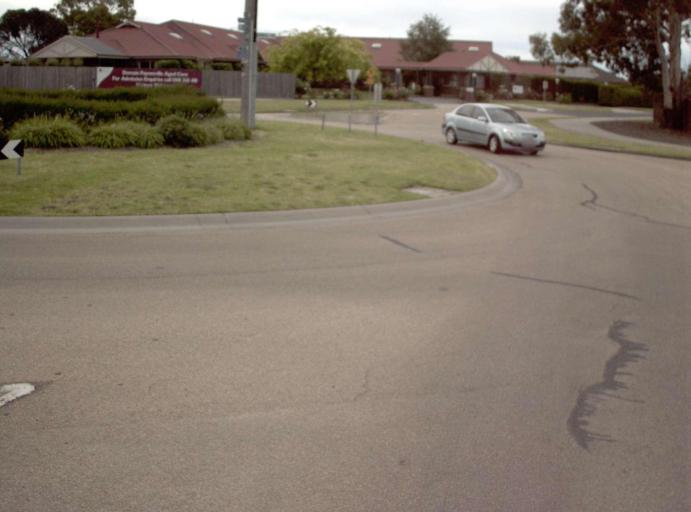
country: AU
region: Victoria
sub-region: East Gippsland
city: Bairnsdale
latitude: -37.9077
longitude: 147.7208
